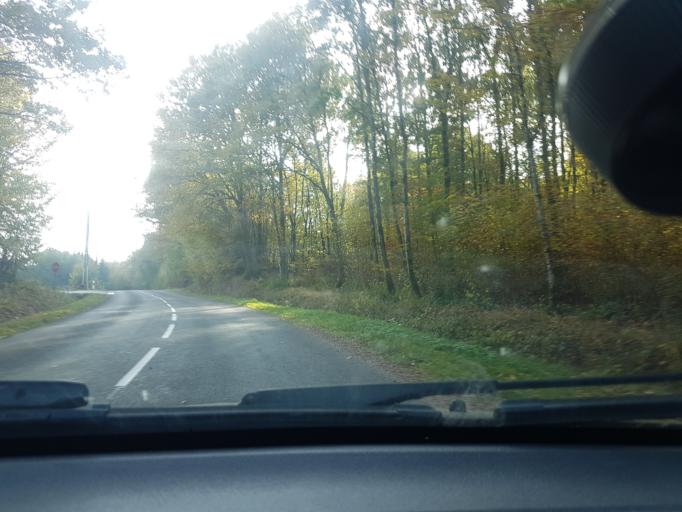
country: FR
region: Franche-Comte
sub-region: Departement de la Haute-Saone
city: Frahier-et-Chatebier
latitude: 47.6696
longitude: 6.7365
